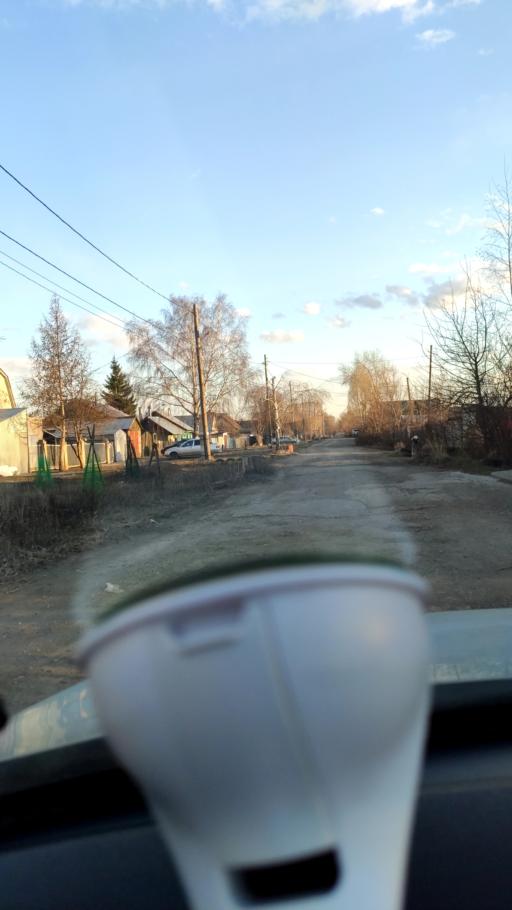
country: RU
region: Samara
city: Smyshlyayevka
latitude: 53.2491
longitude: 50.3429
